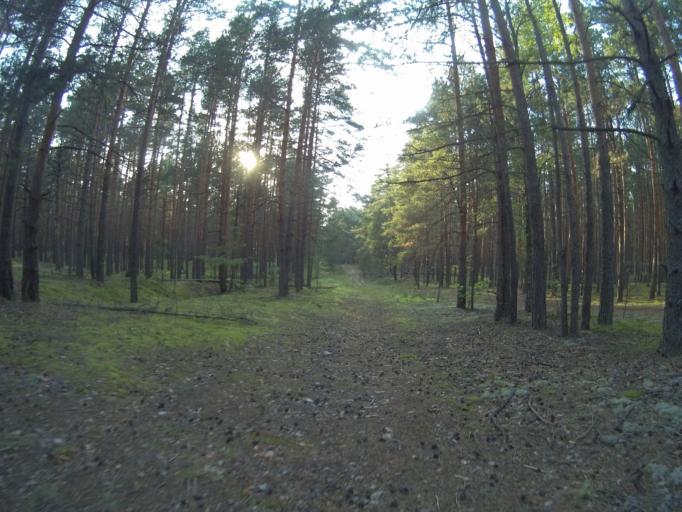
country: RU
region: Vladimir
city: Kommunar
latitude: 56.0796
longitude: 40.4349
